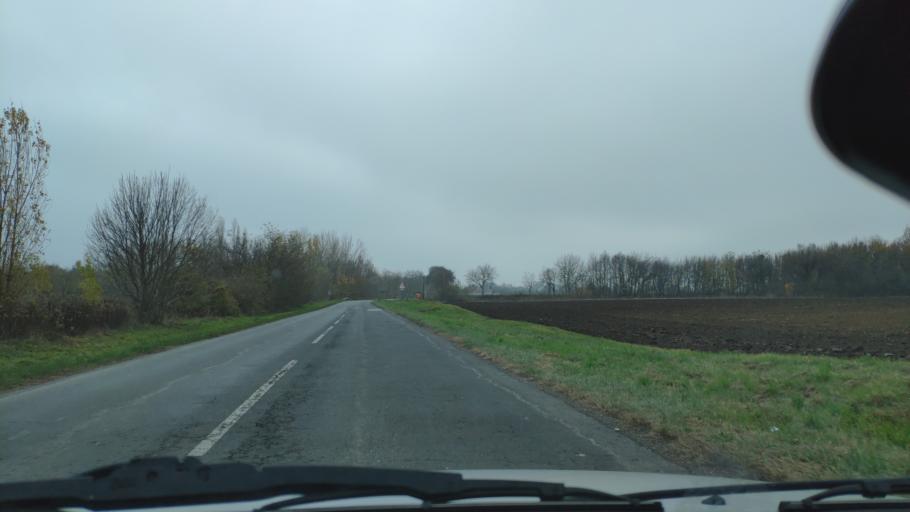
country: HU
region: Somogy
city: Balatonbereny
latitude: 46.6823
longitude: 17.2836
